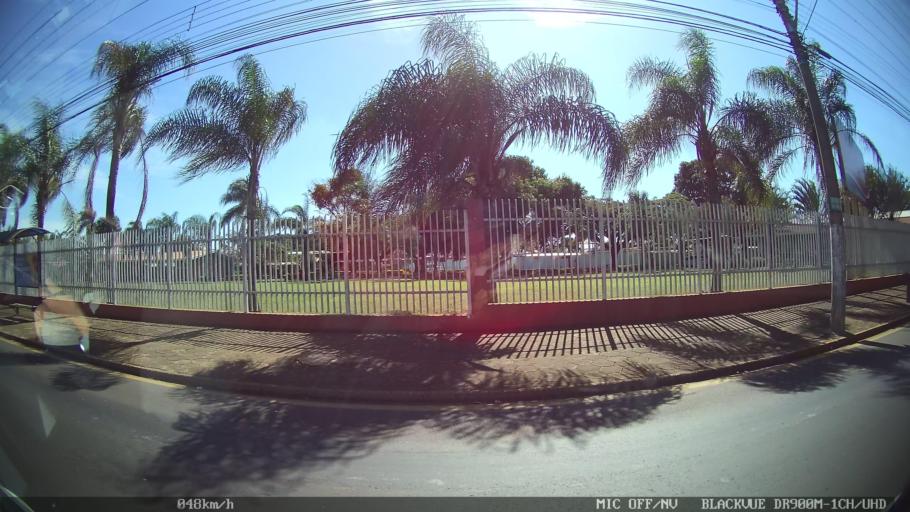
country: BR
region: Sao Paulo
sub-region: Franca
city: Franca
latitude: -20.5450
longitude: -47.4272
